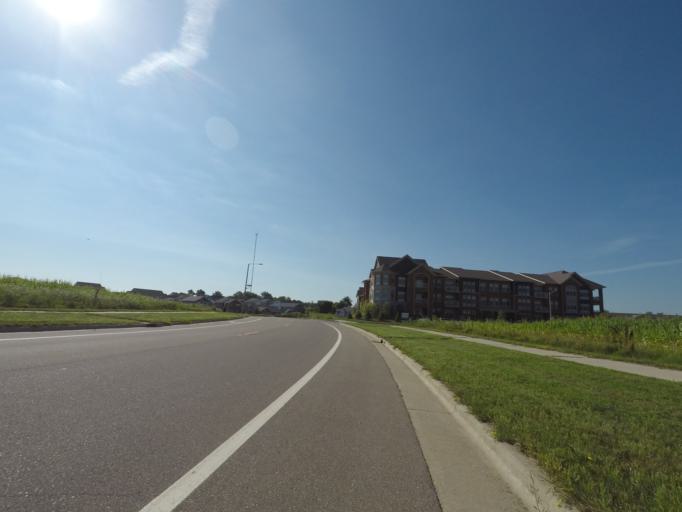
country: US
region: Wisconsin
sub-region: Dane County
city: Middleton
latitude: 43.0662
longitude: -89.5535
